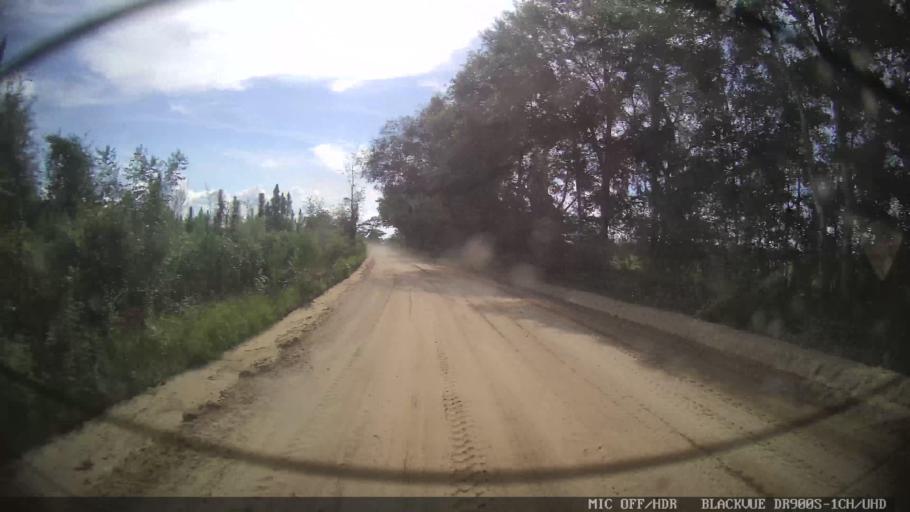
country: US
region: Georgia
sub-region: Echols County
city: Statenville
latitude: 30.6245
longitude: -83.1914
